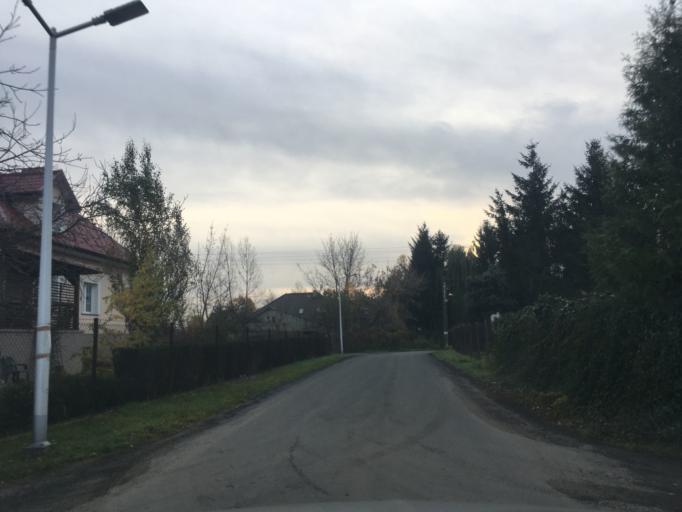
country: PL
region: Masovian Voivodeship
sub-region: Powiat pruszkowski
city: Brwinow
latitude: 52.1433
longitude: 20.7323
